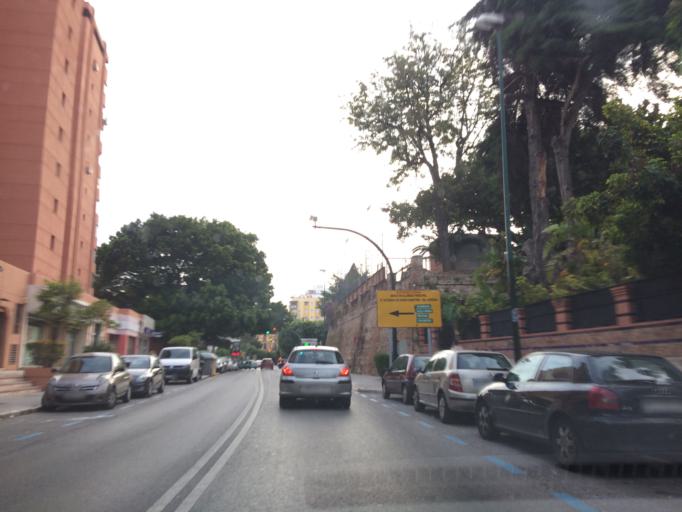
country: ES
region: Andalusia
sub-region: Provincia de Malaga
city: Malaga
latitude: 36.7216
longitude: -4.4044
